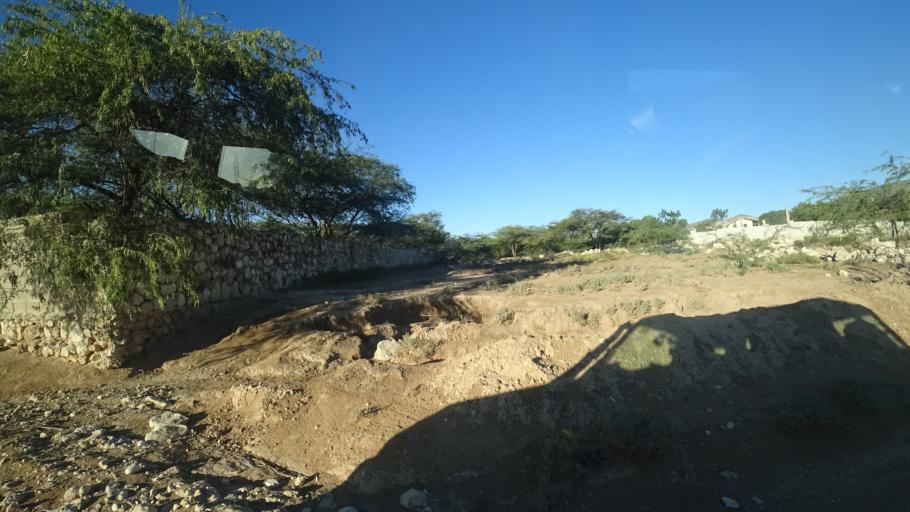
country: HT
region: Ouest
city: Croix des Bouquets
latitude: 18.6614
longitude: -72.2230
